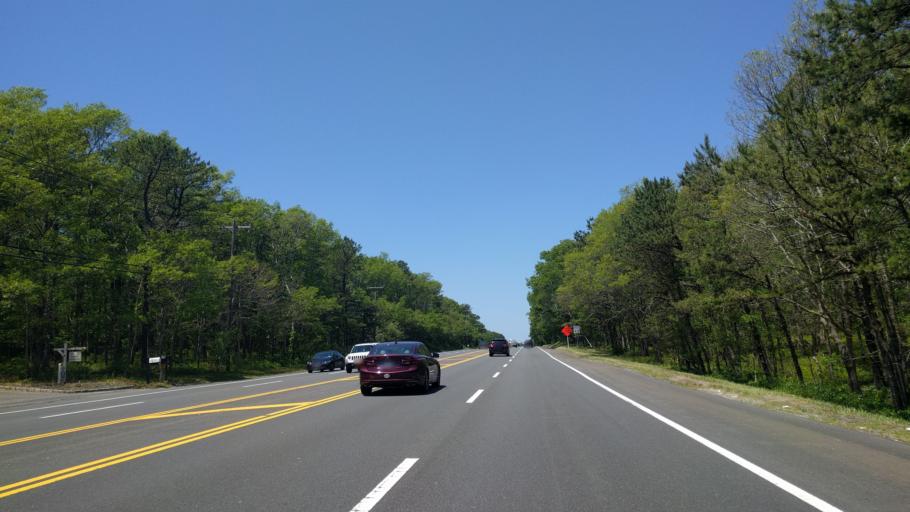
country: US
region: New York
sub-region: Suffolk County
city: Manorville
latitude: 40.8654
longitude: -72.7824
